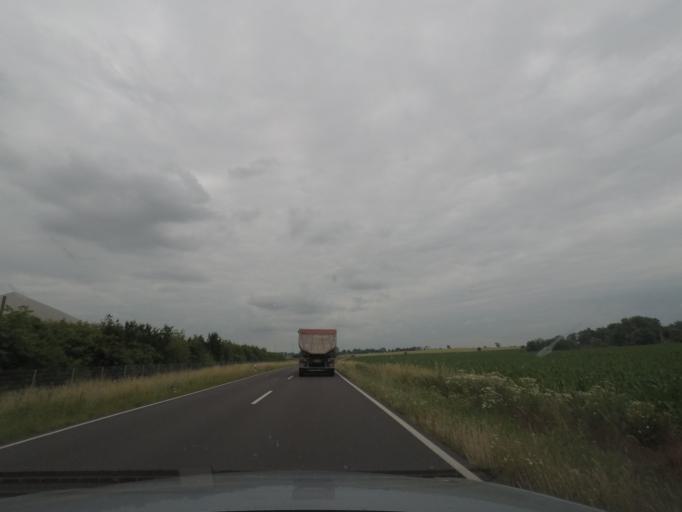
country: DE
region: Saxony-Anhalt
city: Erxleben
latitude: 52.2190
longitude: 11.3021
